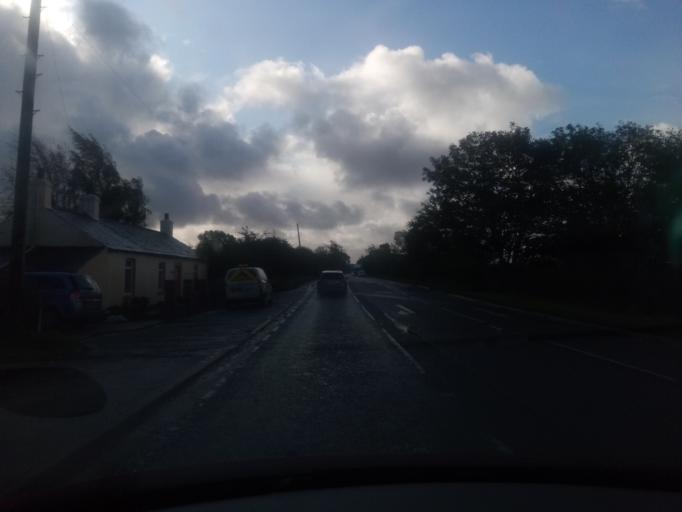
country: GB
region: England
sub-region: Cumbria
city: Carlisle
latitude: 54.9506
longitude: -2.9432
